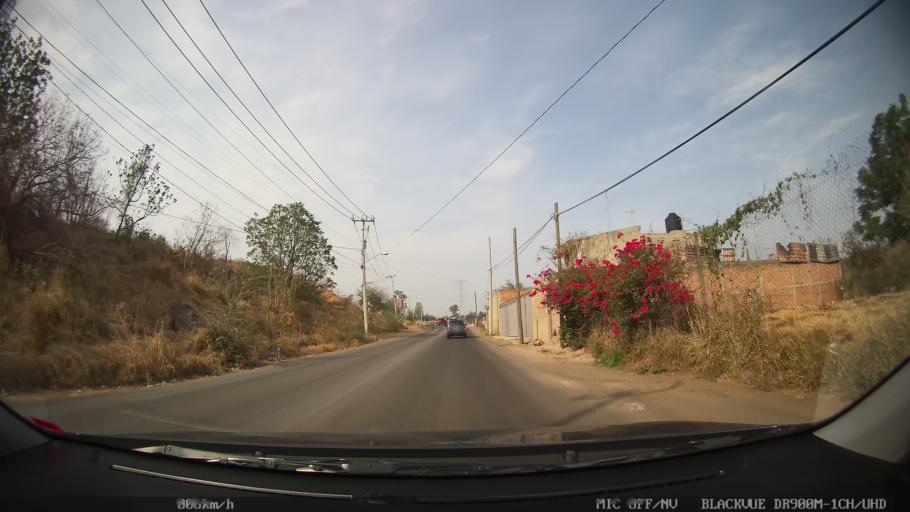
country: MX
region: Jalisco
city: Tonala
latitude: 20.6215
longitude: -103.2220
